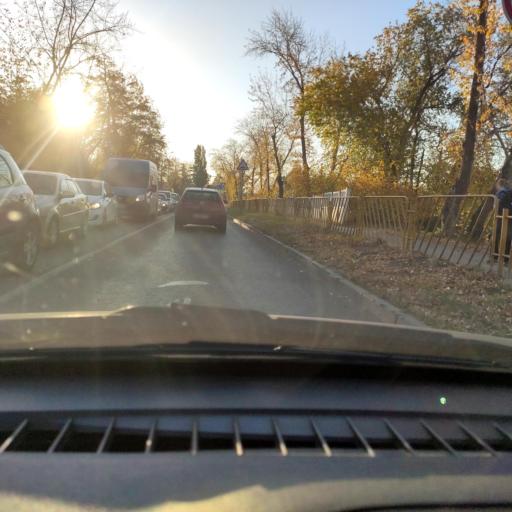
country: RU
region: Samara
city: Tol'yatti
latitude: 53.4777
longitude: 49.3661
